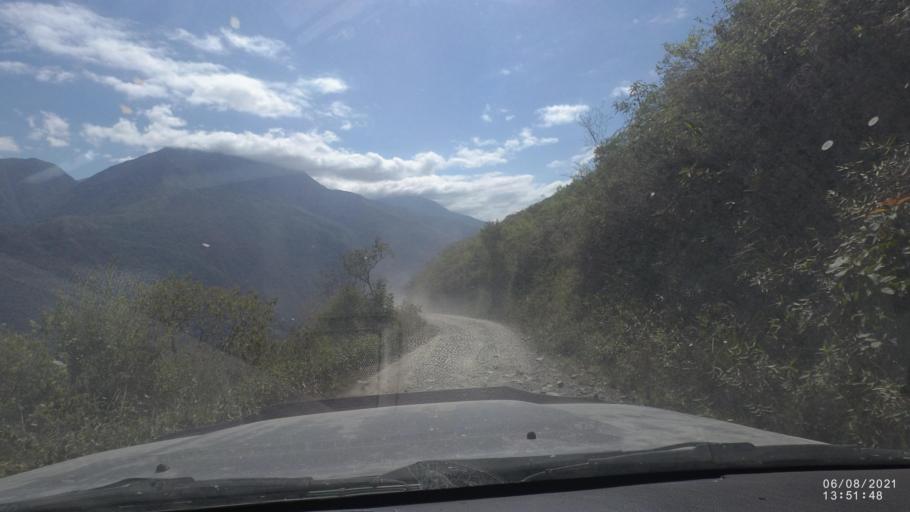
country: BO
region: La Paz
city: Quime
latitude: -16.6513
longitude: -66.7271
